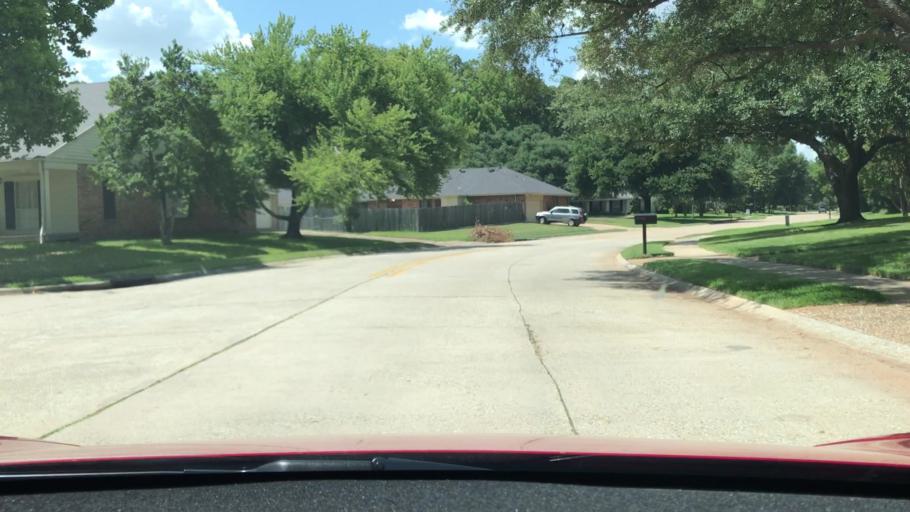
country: US
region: Louisiana
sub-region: Bossier Parish
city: Bossier City
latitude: 32.4267
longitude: -93.7278
